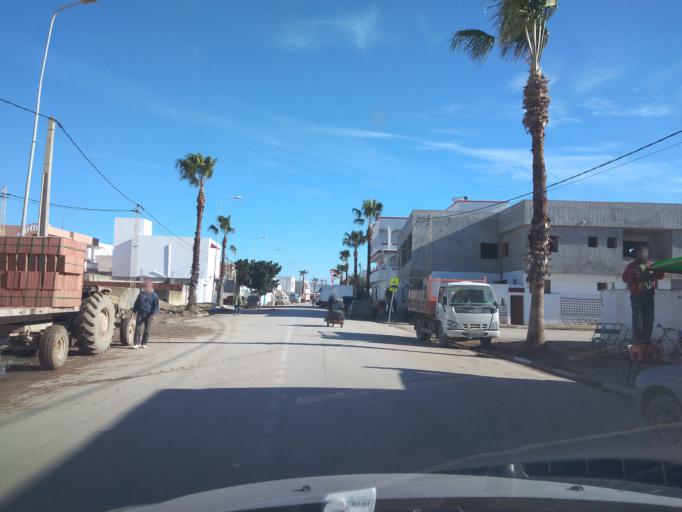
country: TN
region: Ariana
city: Qal'at al Andalus
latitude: 37.0622
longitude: 10.1213
